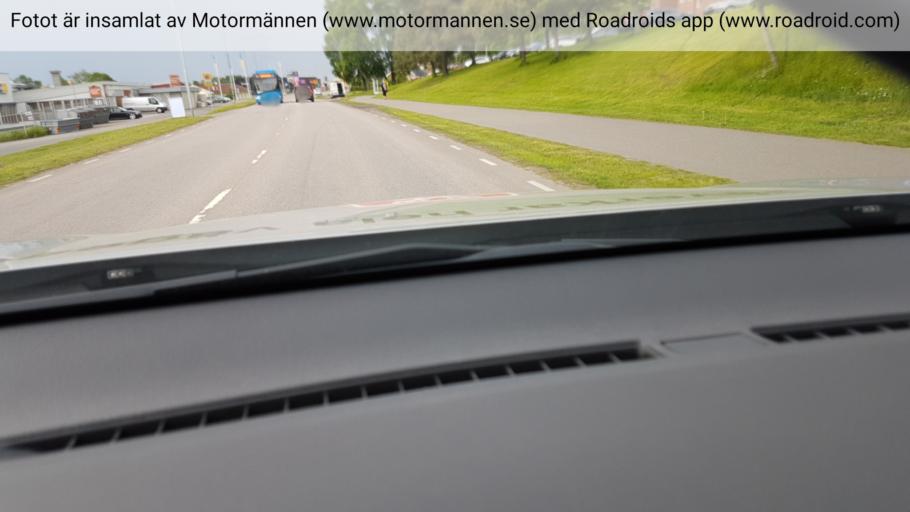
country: SE
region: Vaestra Goetaland
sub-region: Skovde Kommun
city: Skoevde
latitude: 58.4063
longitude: 13.8660
